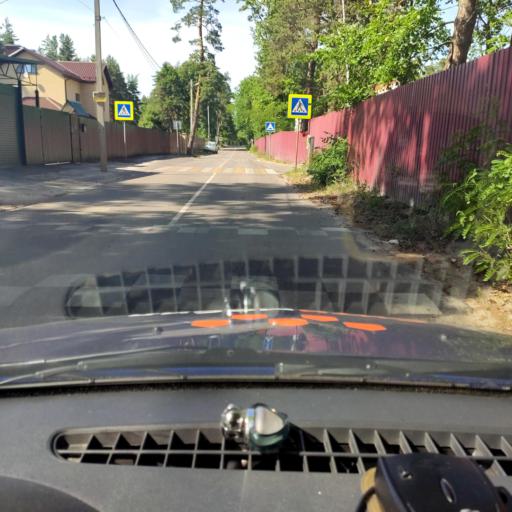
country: RU
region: Voronezj
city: Somovo
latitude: 51.7551
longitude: 39.3661
